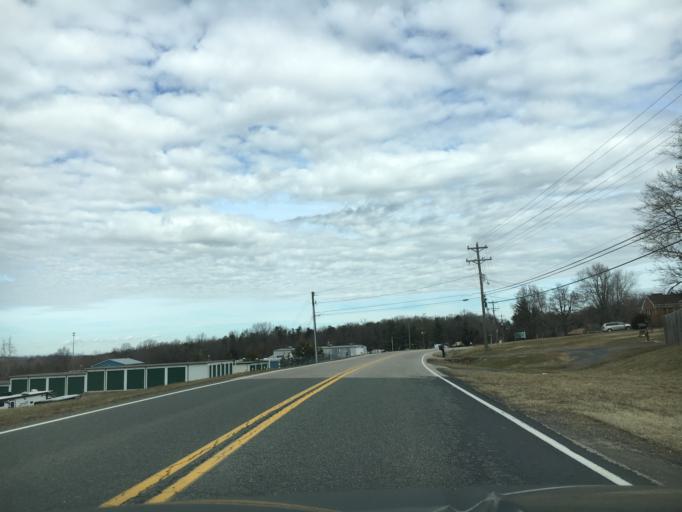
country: US
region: Virginia
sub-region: Augusta County
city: Crimora
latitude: 38.1382
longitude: -78.8451
